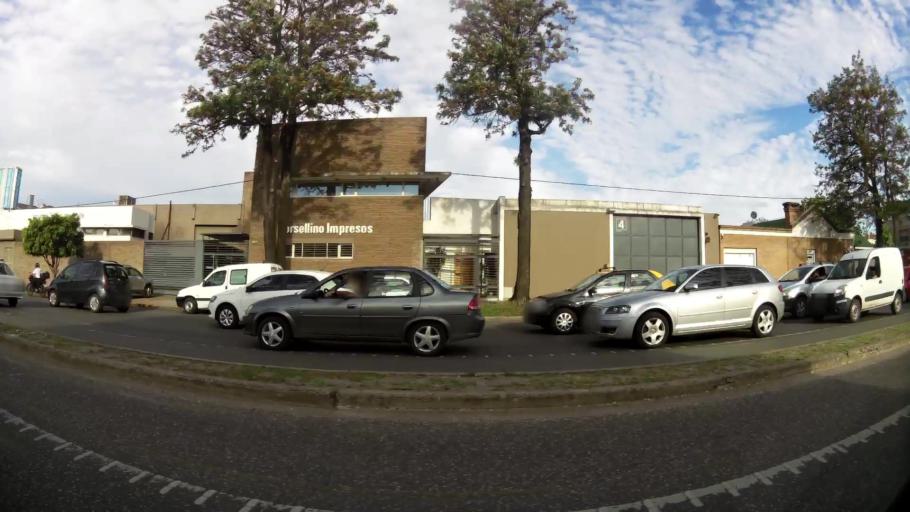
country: AR
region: Santa Fe
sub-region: Departamento de Rosario
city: Rosario
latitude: -32.9759
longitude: -60.6695
